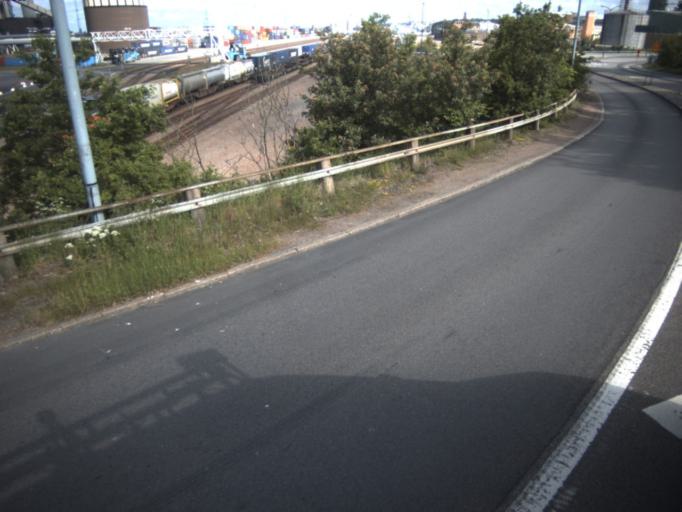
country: SE
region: Skane
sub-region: Helsingborg
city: Helsingborg
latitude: 56.0321
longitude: 12.7001
